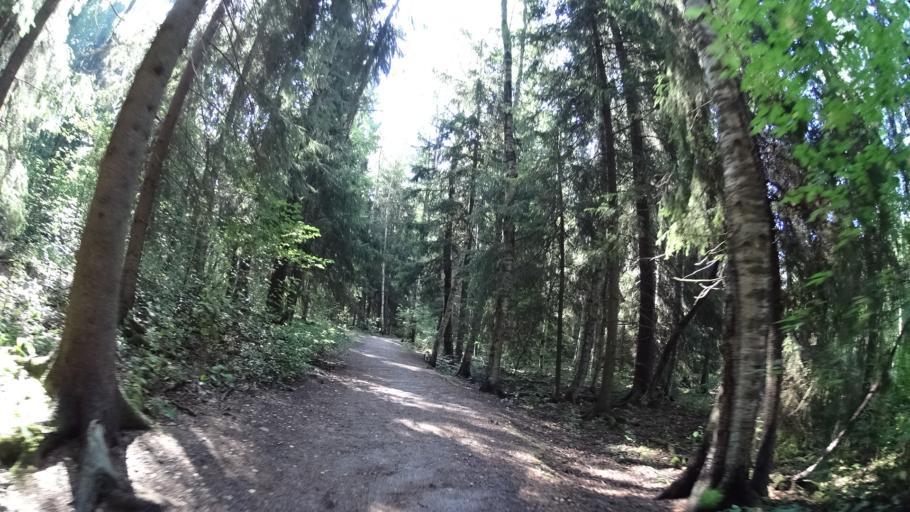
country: FI
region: Uusimaa
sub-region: Helsinki
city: Teekkarikylae
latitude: 60.2627
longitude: 24.8638
